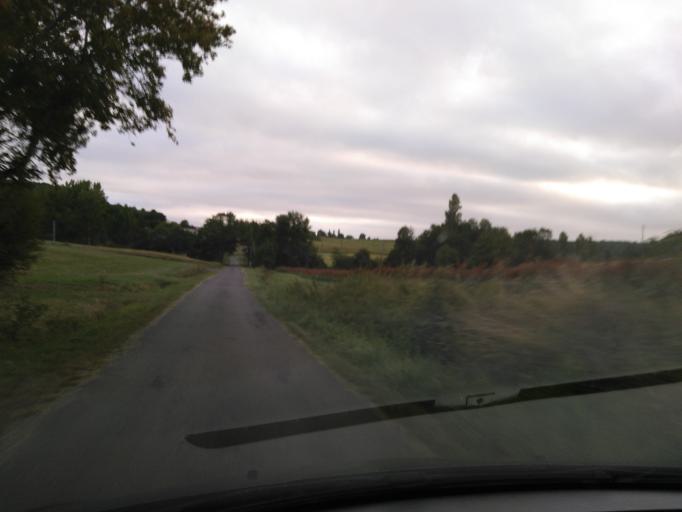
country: FR
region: Aquitaine
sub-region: Departement du Lot-et-Garonne
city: Saint-Hilaire
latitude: 44.5034
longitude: 0.6789
